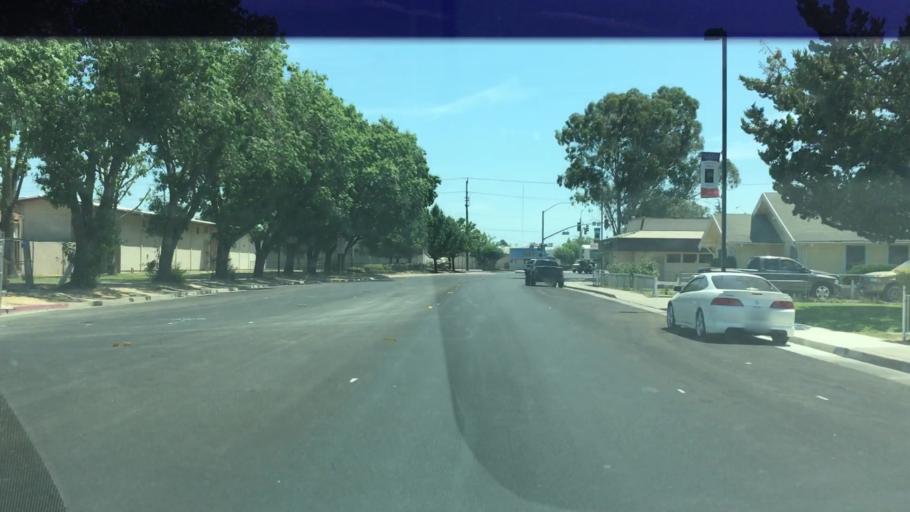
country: US
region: California
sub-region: Sacramento County
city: Galt
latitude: 38.2561
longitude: -121.3004
